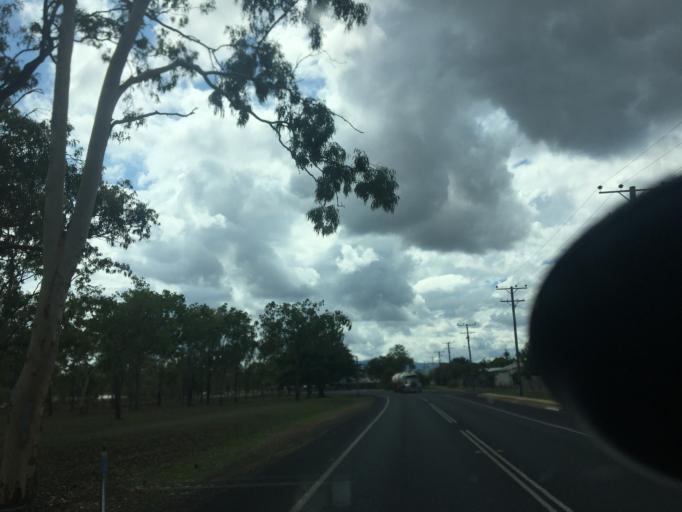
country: AU
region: Queensland
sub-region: Tablelands
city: Mareeba
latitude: -17.0097
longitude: 145.4269
